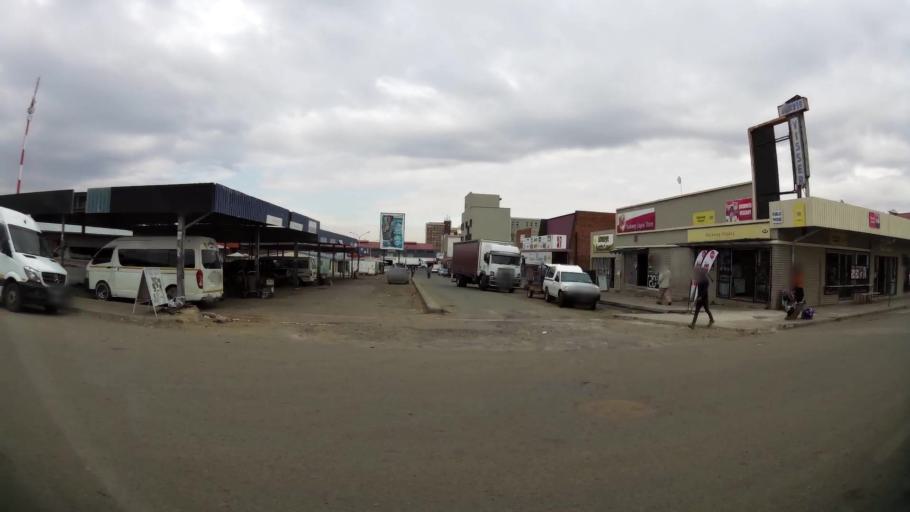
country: ZA
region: Orange Free State
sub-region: Fezile Dabi District Municipality
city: Kroonstad
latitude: -27.6608
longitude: 27.2333
